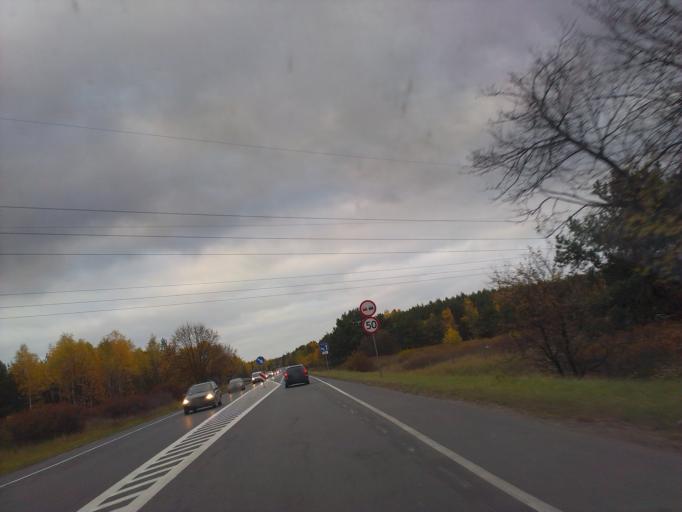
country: PL
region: Kujawsko-Pomorskie
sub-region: Powiat torunski
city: Lysomice
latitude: 53.0503
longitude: 18.6170
